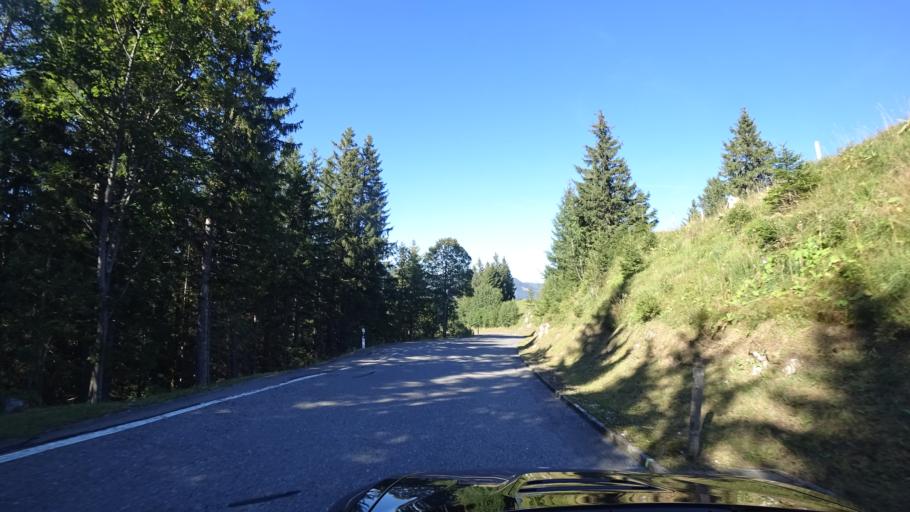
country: CH
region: Obwalden
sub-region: Obwalden
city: Lungern
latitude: 46.8250
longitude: 8.0995
